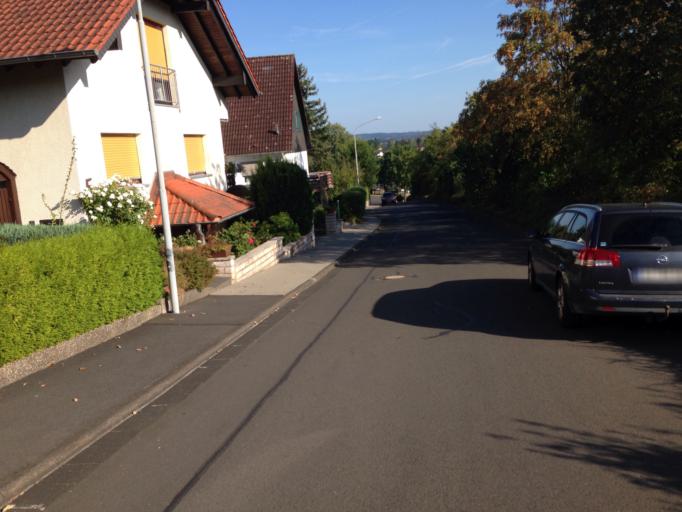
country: DE
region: Hesse
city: Lollar
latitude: 50.6376
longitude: 8.6667
